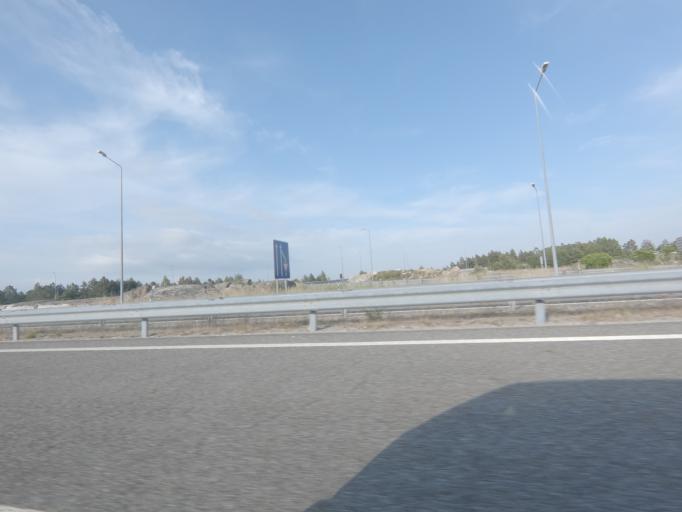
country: PT
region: Vila Real
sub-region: Vila Pouca de Aguiar
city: Vila Pouca de Aguiar
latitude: 41.5071
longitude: -7.6570
